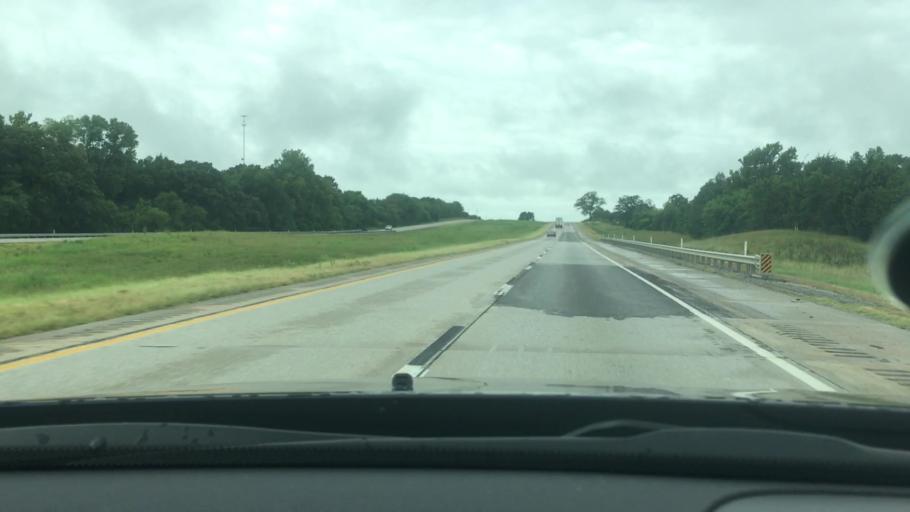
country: US
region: Oklahoma
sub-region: Bryan County
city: Durant
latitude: 34.1842
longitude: -96.2467
